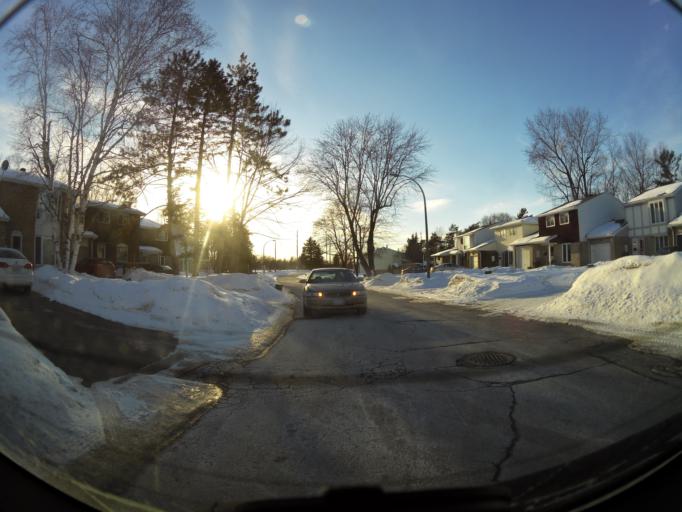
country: CA
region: Ontario
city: Ottawa
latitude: 45.4283
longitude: -75.5708
